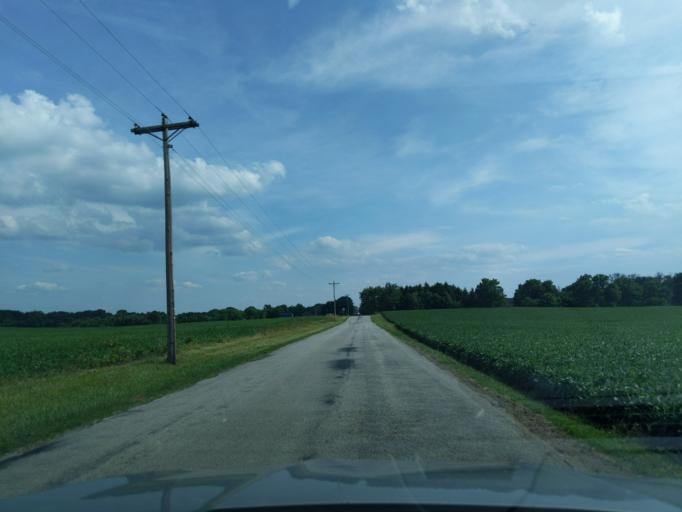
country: US
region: Indiana
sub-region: Decatur County
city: Greensburg
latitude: 39.3062
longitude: -85.4702
